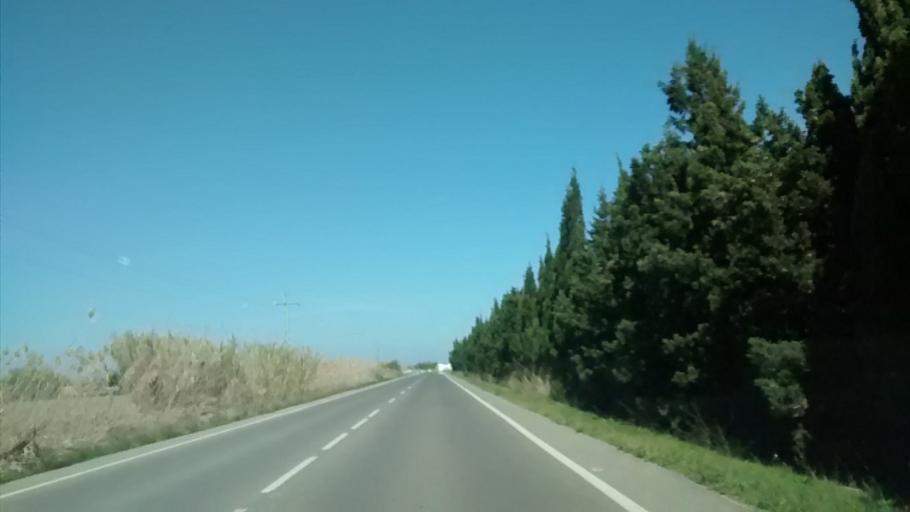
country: ES
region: Catalonia
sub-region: Provincia de Tarragona
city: Deltebre
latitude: 40.7100
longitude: 0.8158
